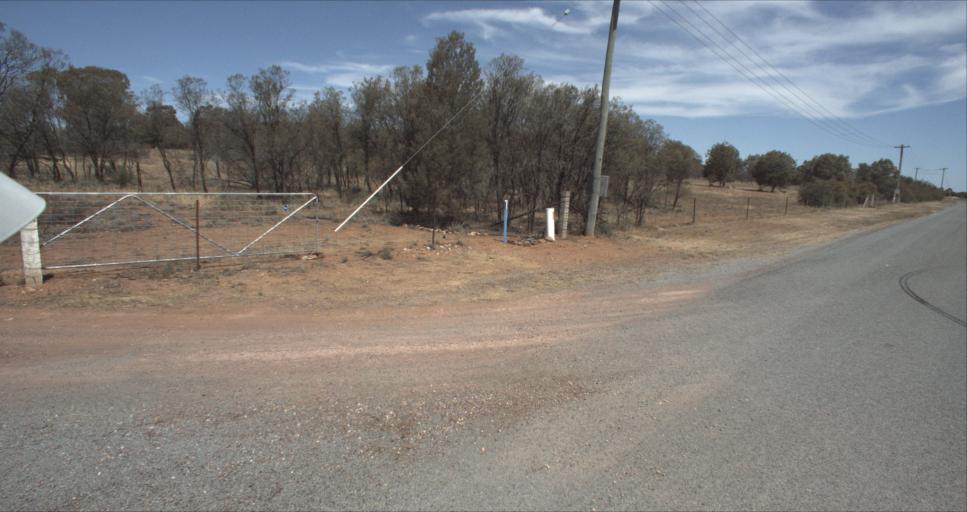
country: AU
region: New South Wales
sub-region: Leeton
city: Leeton
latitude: -34.5757
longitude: 146.4342
